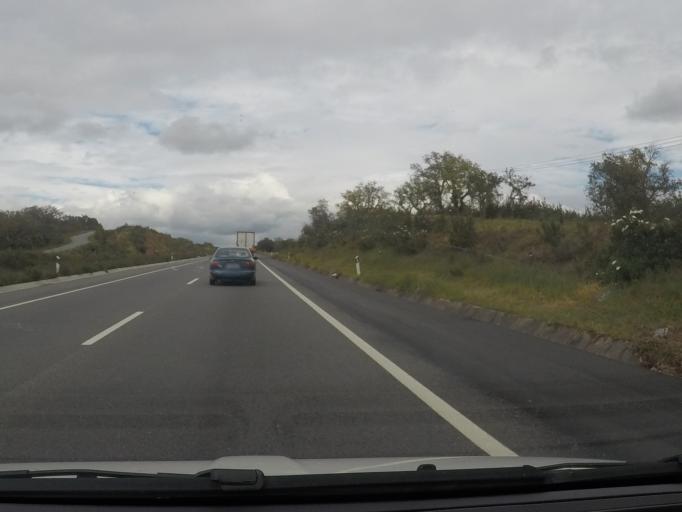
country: PT
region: Setubal
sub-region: Santiago do Cacem
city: Santiago do Cacem
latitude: 38.0678
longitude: -8.6887
